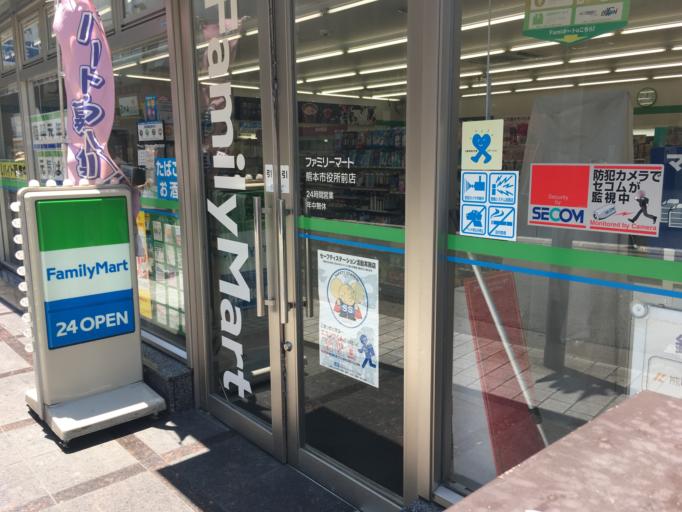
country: JP
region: Kumamoto
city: Kumamoto
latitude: 32.8026
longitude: 130.7079
